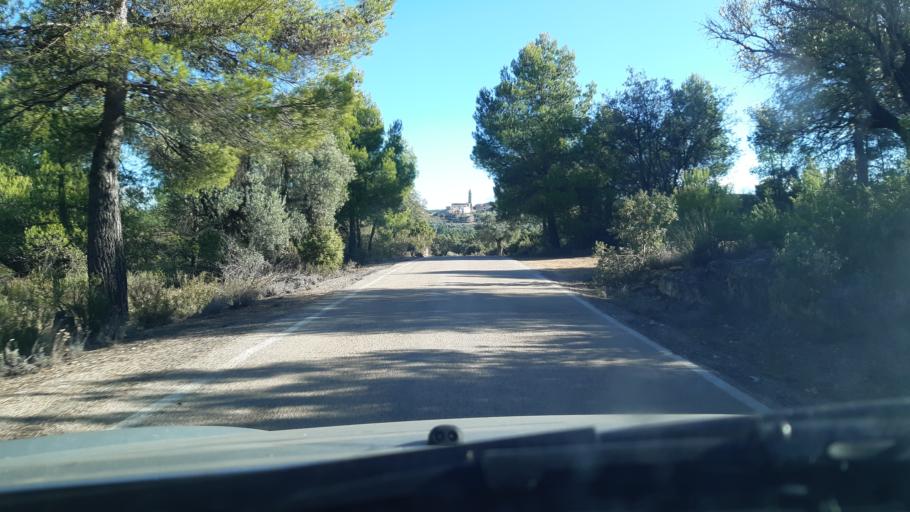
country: ES
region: Aragon
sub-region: Provincia de Teruel
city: Fornoles
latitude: 40.9045
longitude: -0.0110
